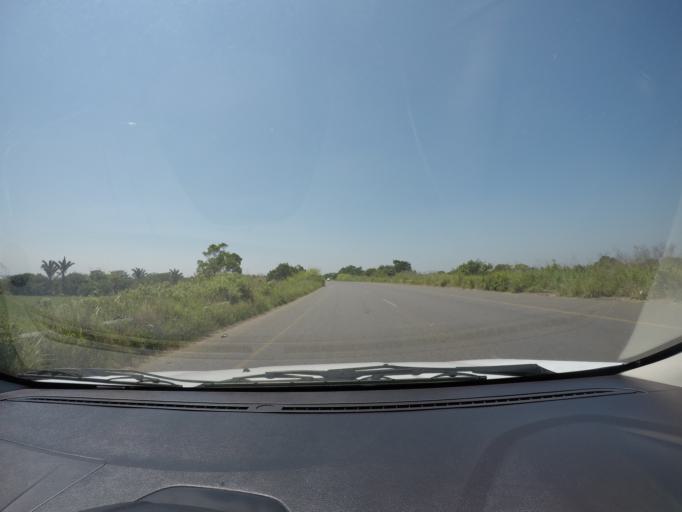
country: ZA
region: KwaZulu-Natal
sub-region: uThungulu District Municipality
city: Empangeni
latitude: -28.8021
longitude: 31.9583
